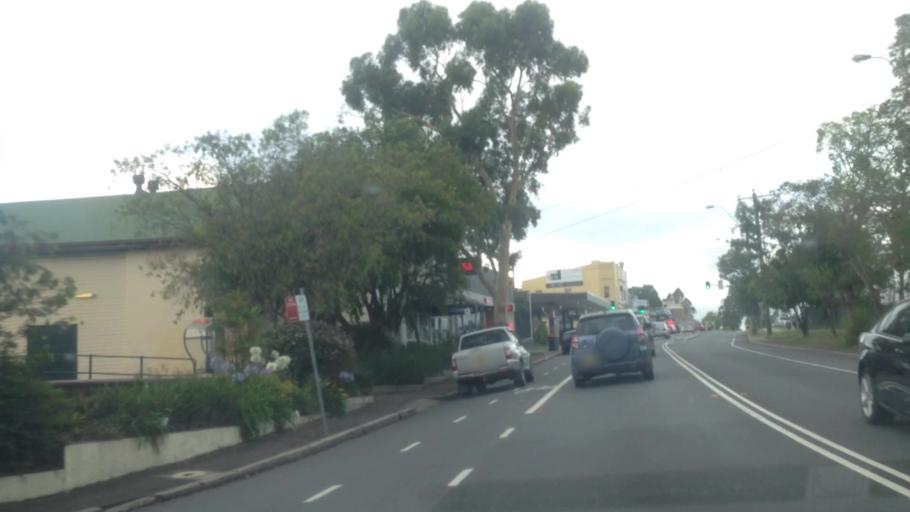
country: AU
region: New South Wales
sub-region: Lake Macquarie Shire
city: Dora Creek
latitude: -33.1083
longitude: 151.4878
